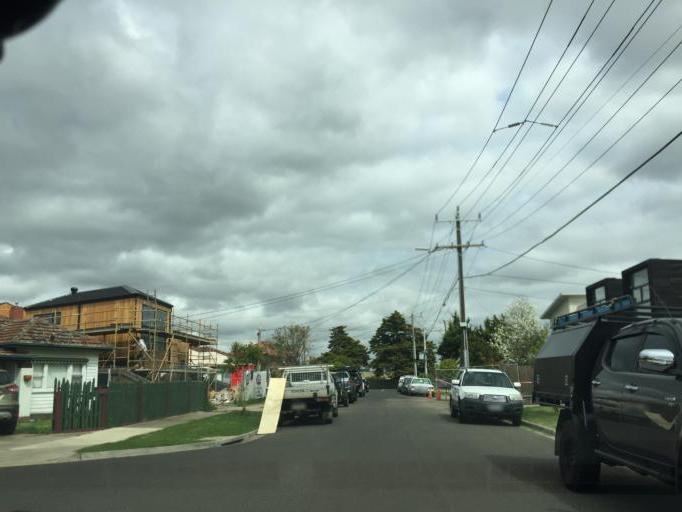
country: AU
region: Victoria
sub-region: Maribyrnong
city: Kingsville
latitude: -37.8138
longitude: 144.8639
